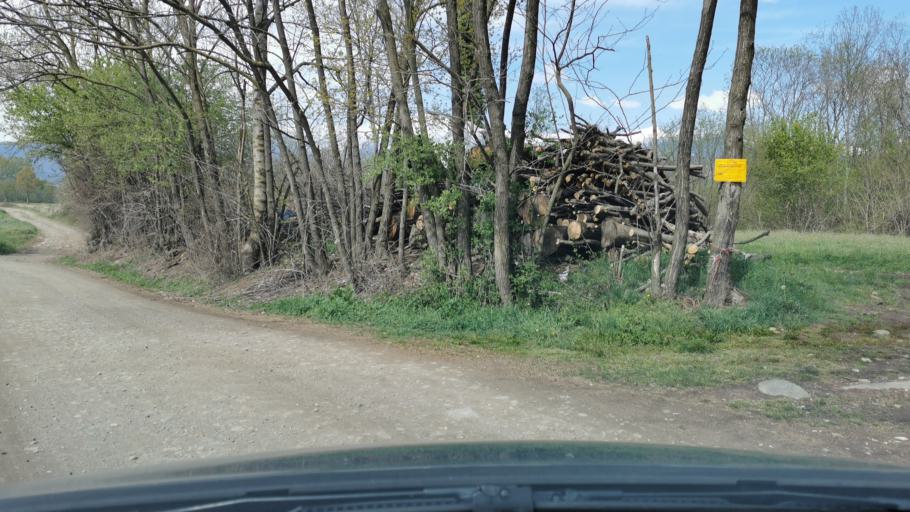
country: IT
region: Piedmont
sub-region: Provincia di Torino
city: San Ponso
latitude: 45.3406
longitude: 7.6719
